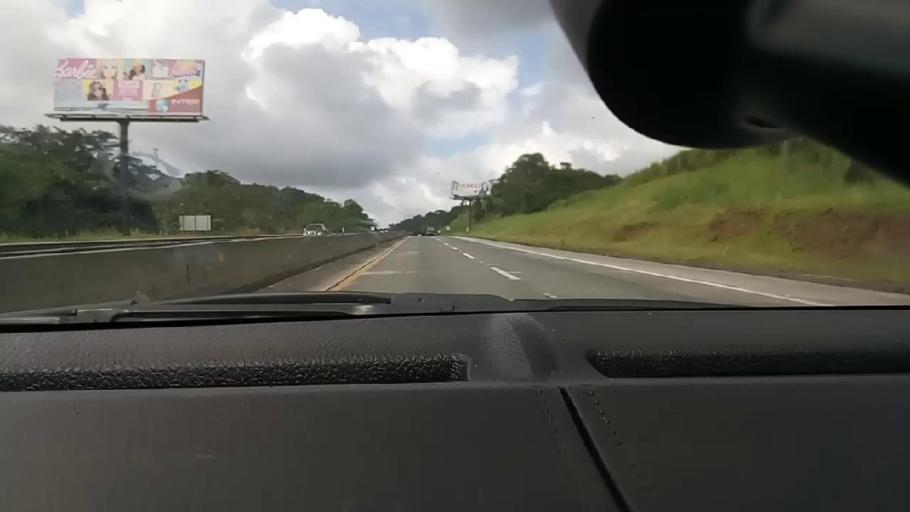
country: PA
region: Colon
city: Quebrada Bonita Adentro
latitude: 9.2809
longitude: -79.7295
